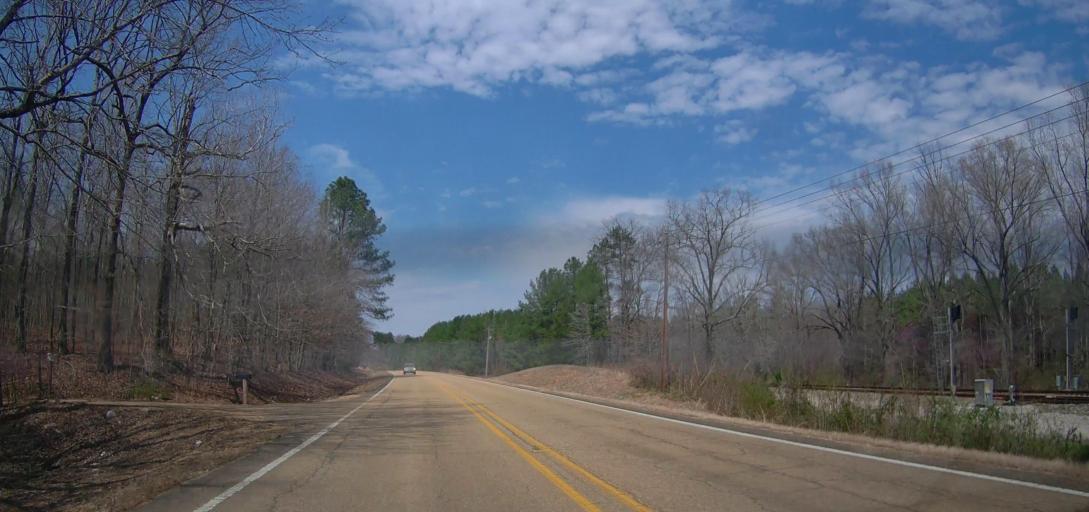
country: US
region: Mississippi
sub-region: Union County
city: New Albany
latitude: 34.6010
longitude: -89.1409
